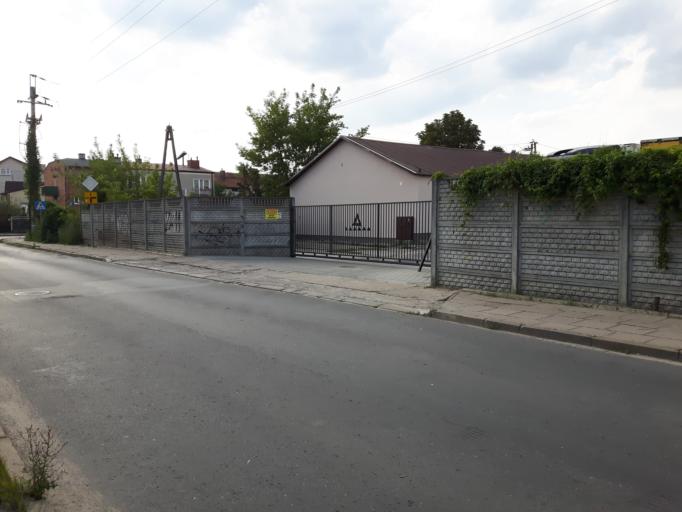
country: PL
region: Masovian Voivodeship
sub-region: Powiat wolominski
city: Zabki
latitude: 52.2871
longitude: 21.1193
